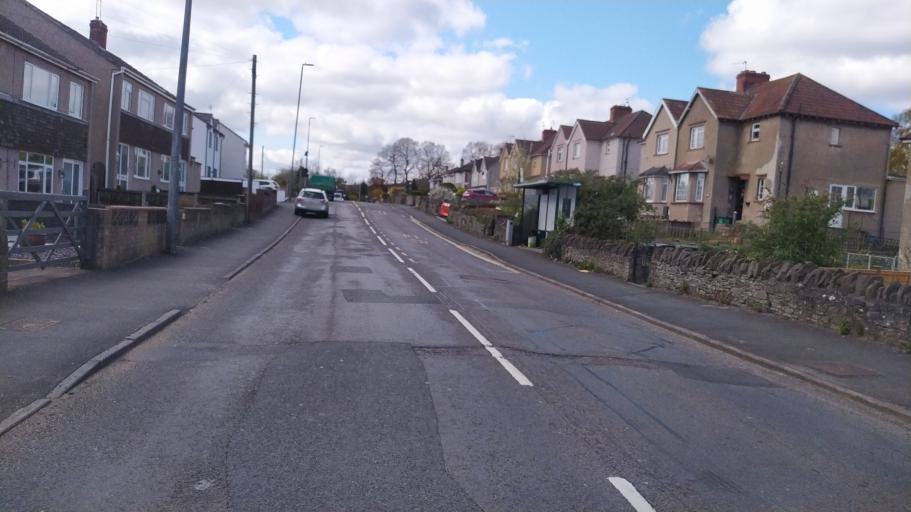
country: GB
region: England
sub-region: South Gloucestershire
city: Kingswood
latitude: 51.4491
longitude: -2.4855
